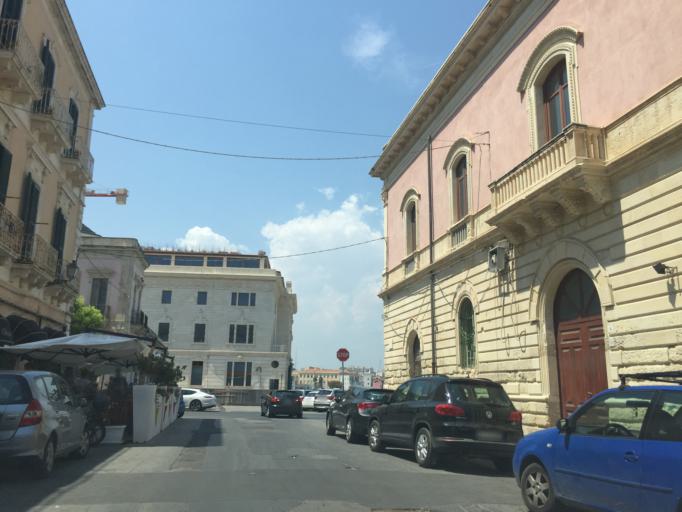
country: IT
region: Sicily
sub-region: Provincia di Siracusa
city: Siracusa
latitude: 37.0657
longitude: 15.2932
